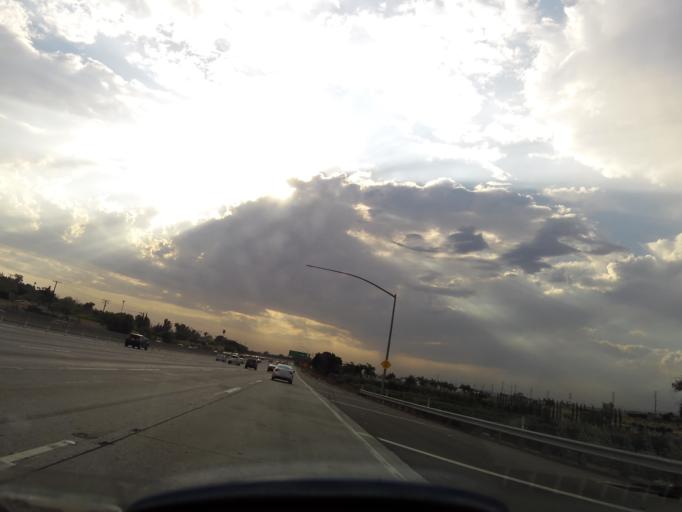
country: US
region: California
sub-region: Orange County
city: Yorba Linda
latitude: 33.8544
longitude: -117.7956
